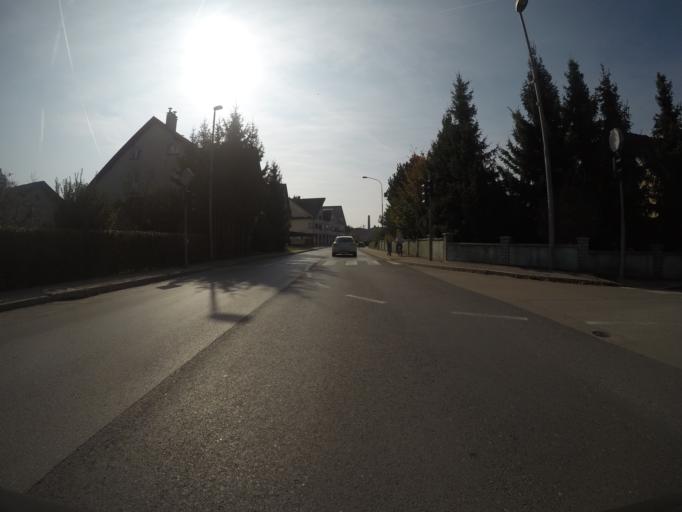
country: SI
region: Kamnik
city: Smarca
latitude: 46.2043
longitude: 14.5971
